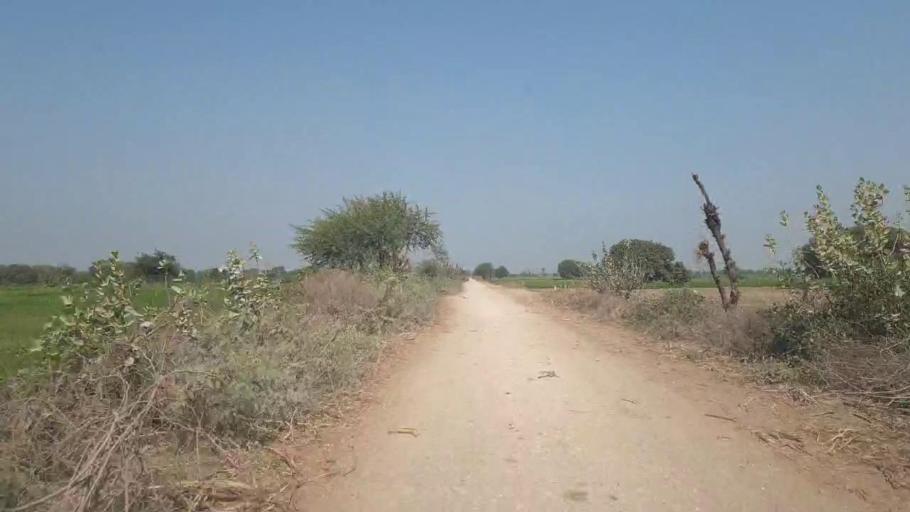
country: PK
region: Sindh
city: Tando Allahyar
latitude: 25.4411
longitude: 68.8499
